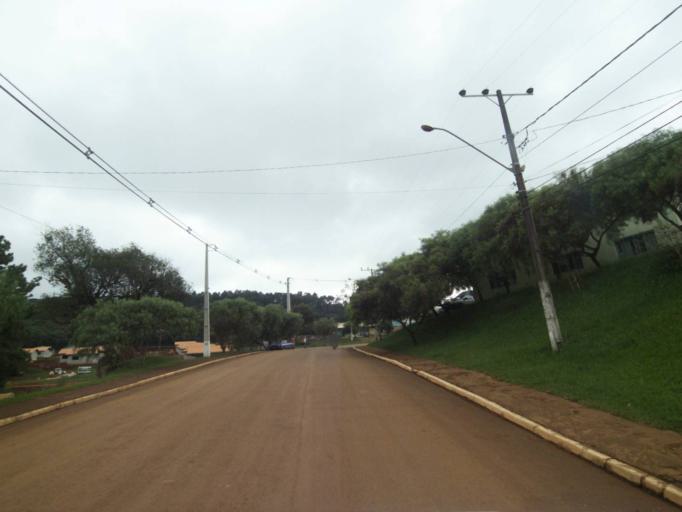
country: BR
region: Parana
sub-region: Pitanga
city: Pitanga
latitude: -24.9400
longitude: -51.8668
